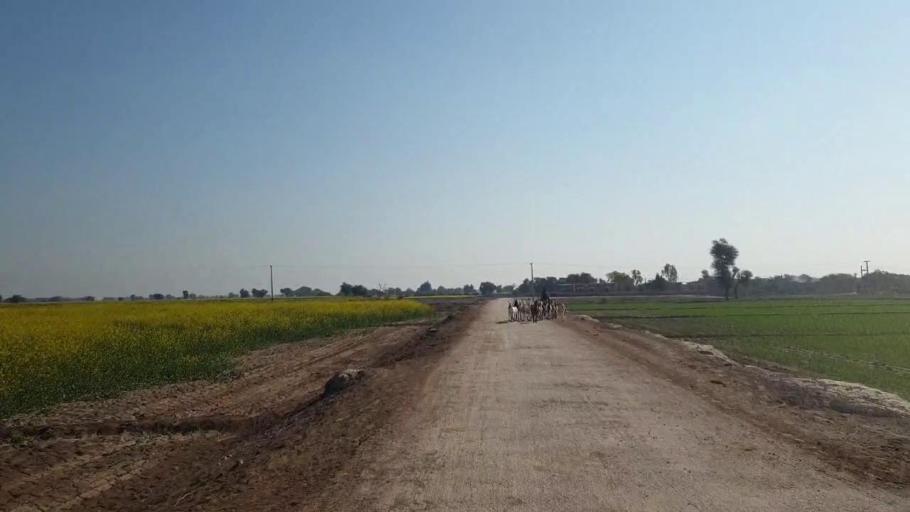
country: PK
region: Sindh
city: Shahpur Chakar
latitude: 26.0820
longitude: 68.6243
